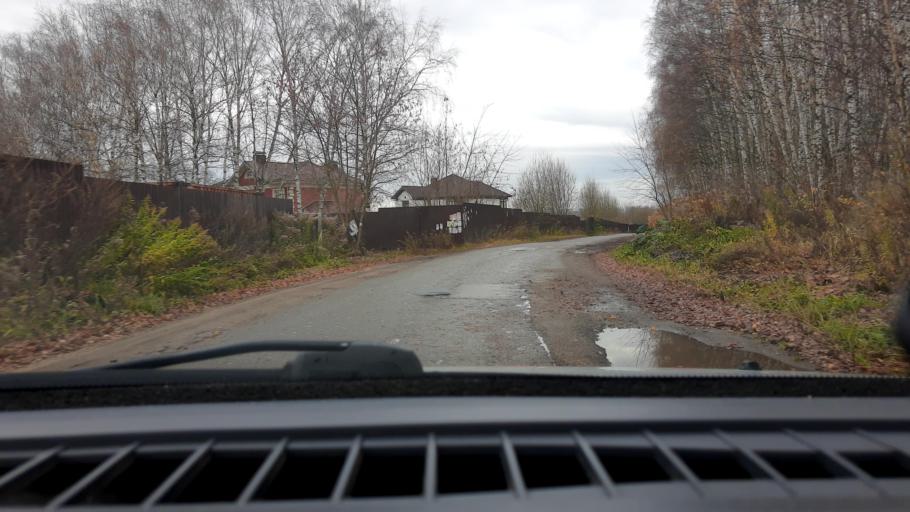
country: RU
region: Nizjnij Novgorod
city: Afonino
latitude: 56.1920
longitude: 44.1045
